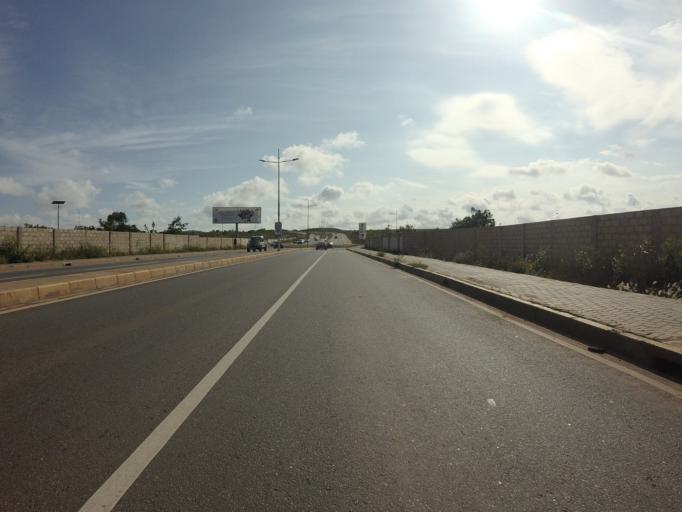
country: GH
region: Greater Accra
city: Medina Estates
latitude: 5.6165
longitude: -0.1542
